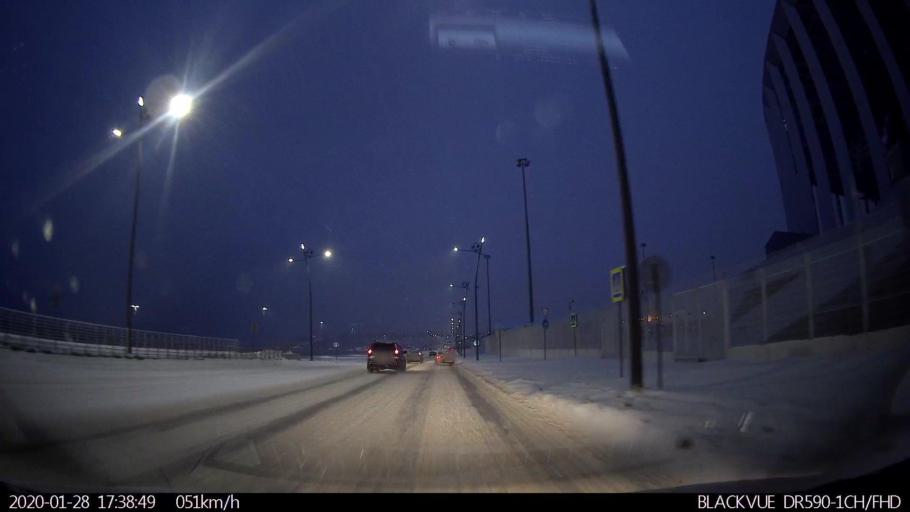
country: RU
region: Nizjnij Novgorod
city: Nizhniy Novgorod
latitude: 56.3392
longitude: 43.9646
